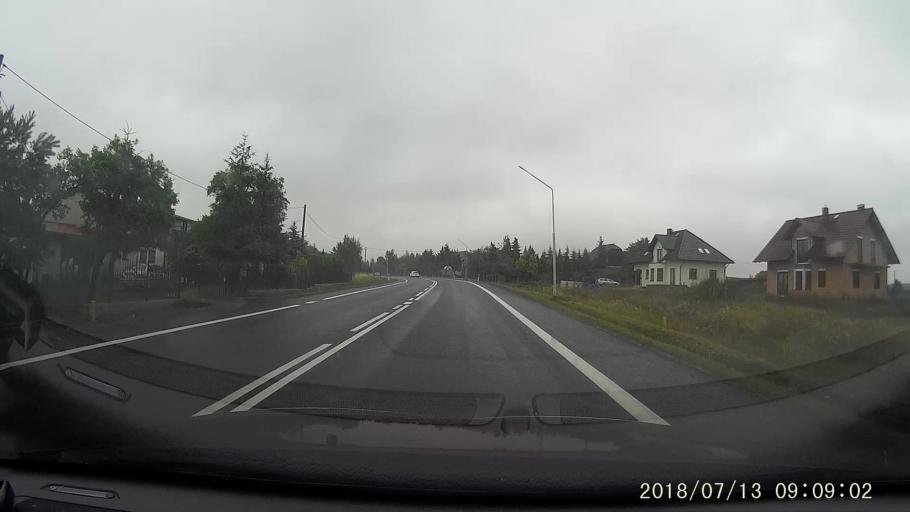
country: PL
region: Lower Silesian Voivodeship
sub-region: Powiat lubanski
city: Siekierczyn
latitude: 51.1524
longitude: 15.1597
